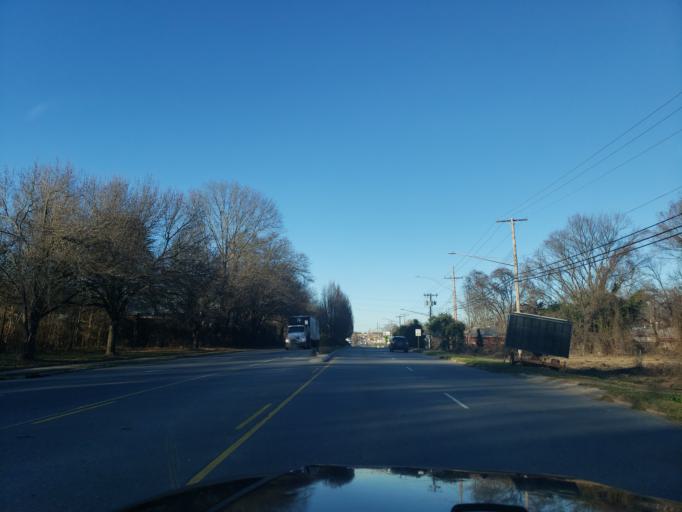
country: US
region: North Carolina
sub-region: Gaston County
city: Gastonia
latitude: 35.2759
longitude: -81.1878
